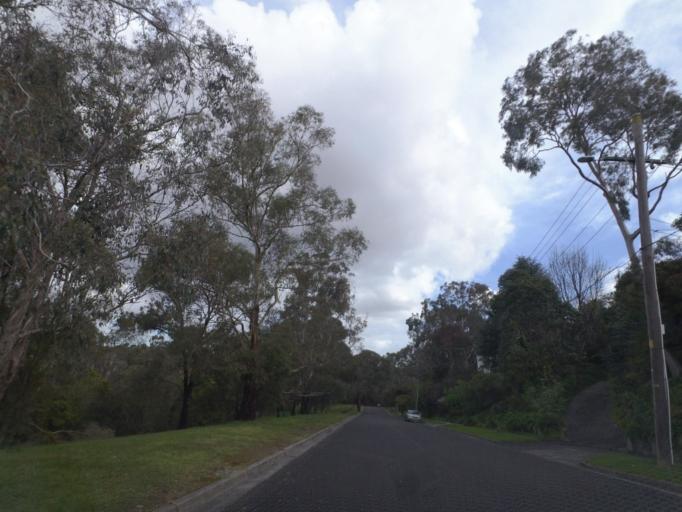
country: AU
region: Victoria
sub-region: Knox
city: Wantirna
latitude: -37.8411
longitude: 145.2118
